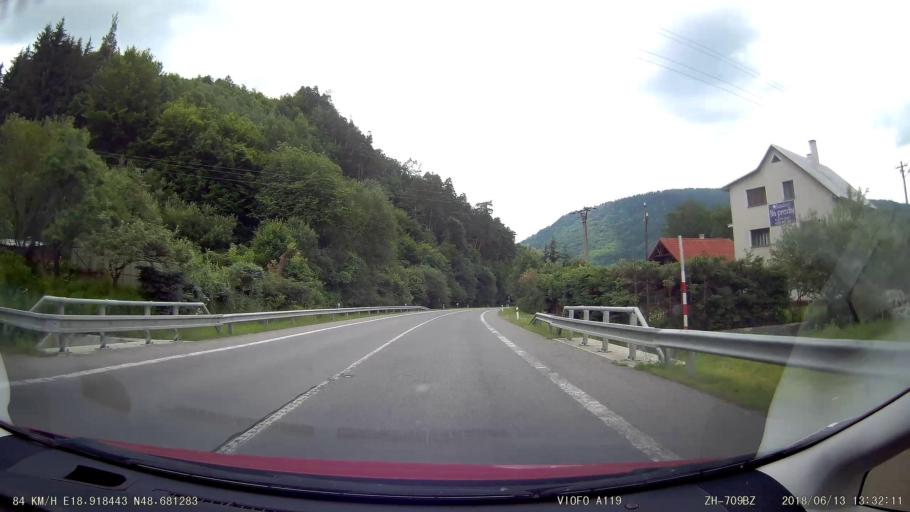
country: SK
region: Banskobystricky
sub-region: Okres Ziar nad Hronom
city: Kremnica
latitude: 48.6810
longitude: 18.9183
